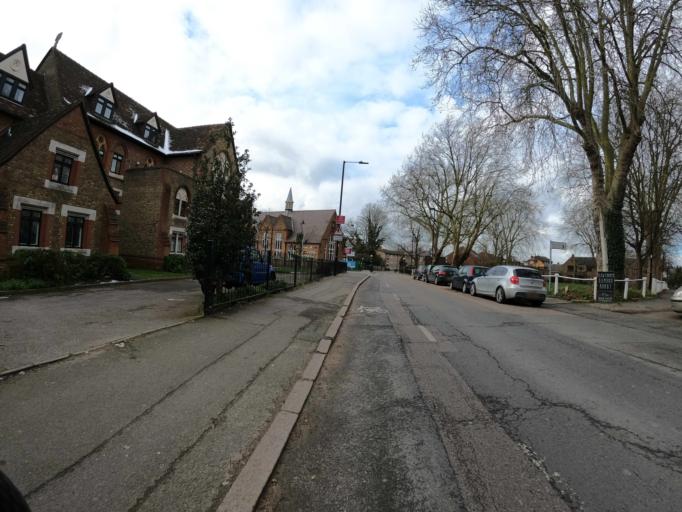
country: GB
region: England
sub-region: Greater London
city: Greenford
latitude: 51.5070
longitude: -0.3397
